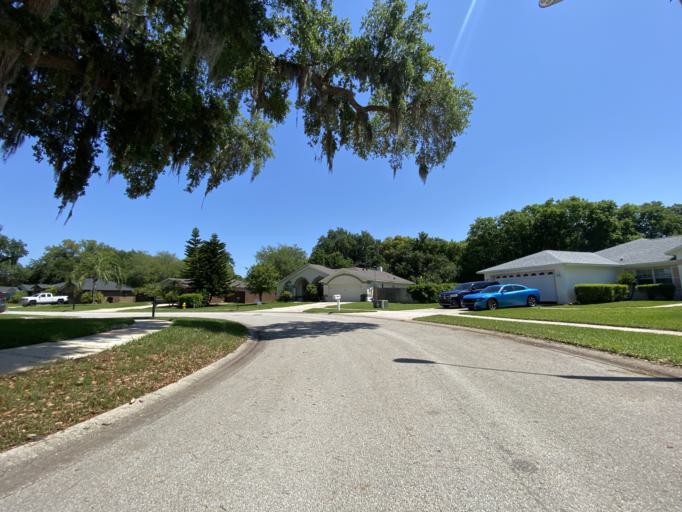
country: US
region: Florida
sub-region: Volusia County
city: Port Orange
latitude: 29.1495
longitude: -81.0037
